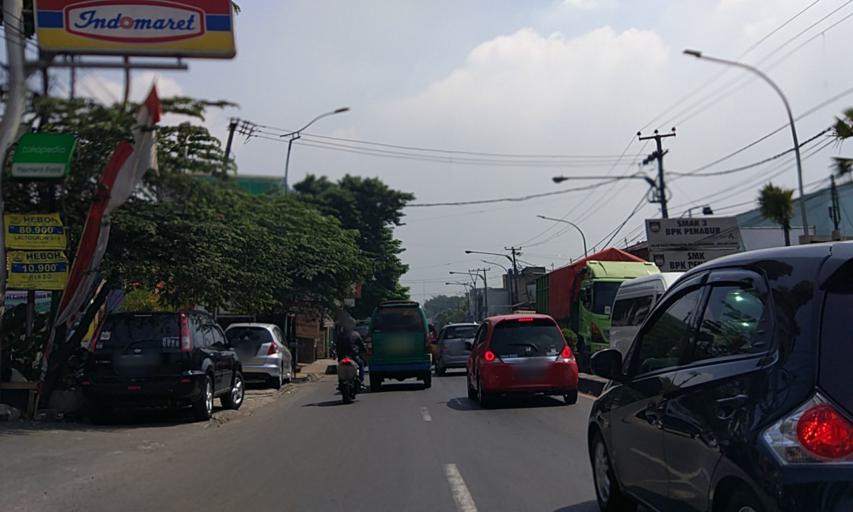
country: ID
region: West Java
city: Cimahi
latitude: -6.9006
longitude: 107.5630
